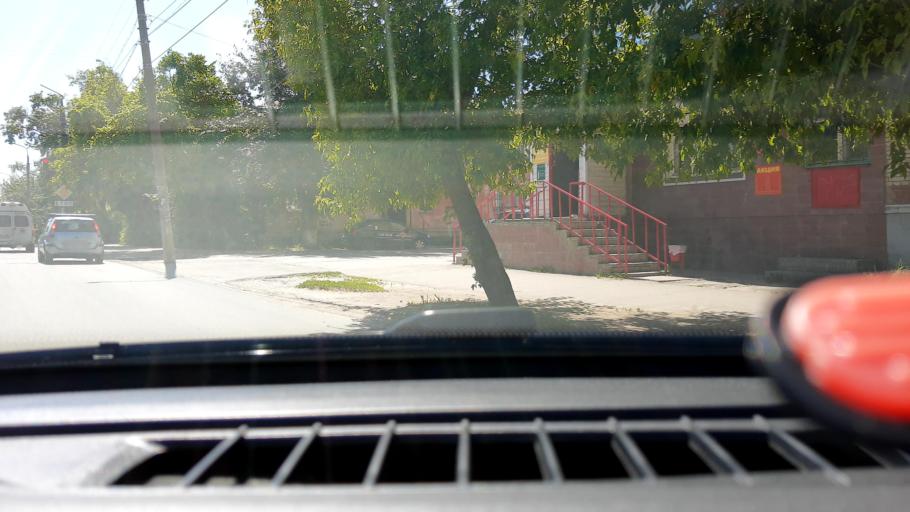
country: RU
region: Nizjnij Novgorod
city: Dzerzhinsk
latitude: 56.2506
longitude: 43.4736
